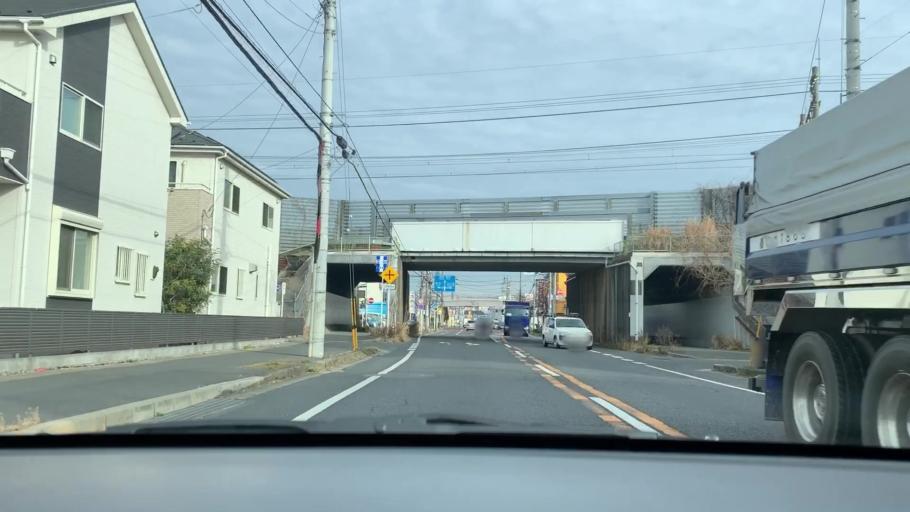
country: JP
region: Chiba
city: Nagareyama
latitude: 35.8429
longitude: 139.8975
